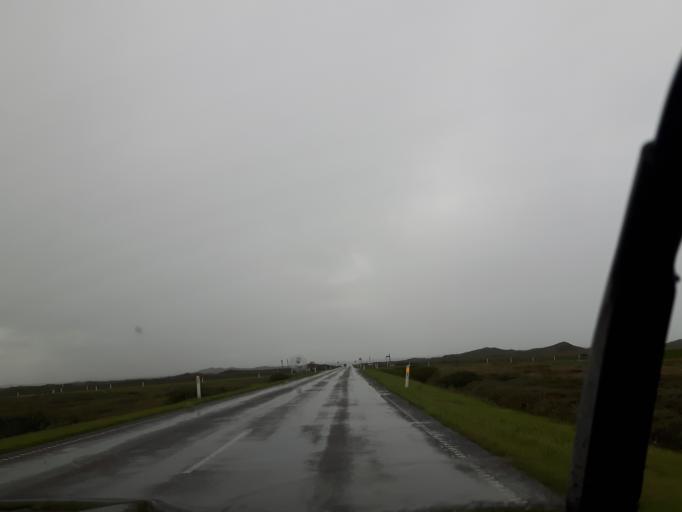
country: DK
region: North Denmark
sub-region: Thisted Kommune
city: Hanstholm
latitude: 57.0030
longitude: 8.4653
